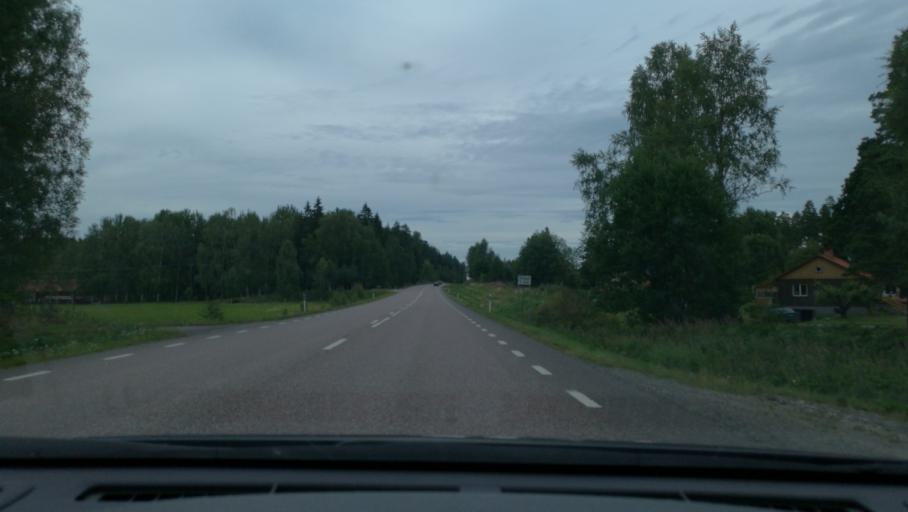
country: SE
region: Soedermanland
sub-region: Katrineholms Kommun
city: Katrineholm
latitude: 59.0365
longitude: 16.2161
